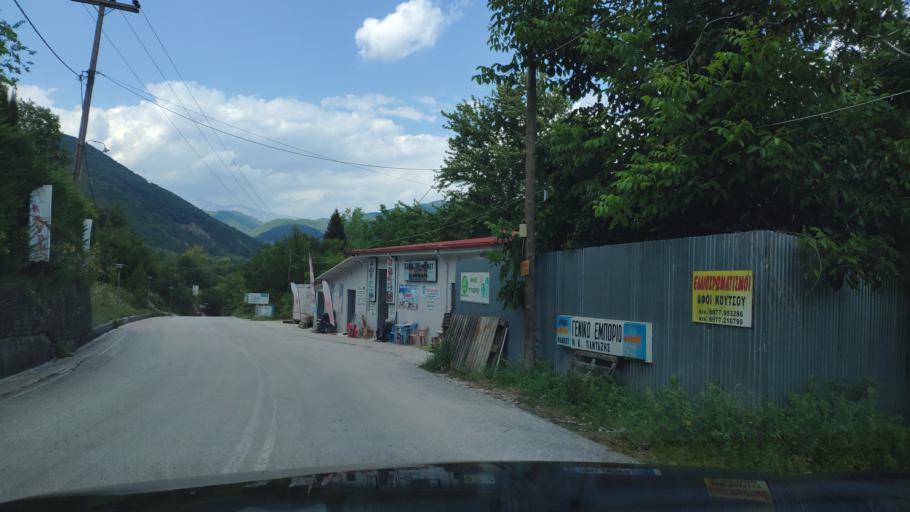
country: GR
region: Epirus
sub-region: Nomos Artas
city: Agios Dimitrios
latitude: 39.4532
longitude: 21.0319
